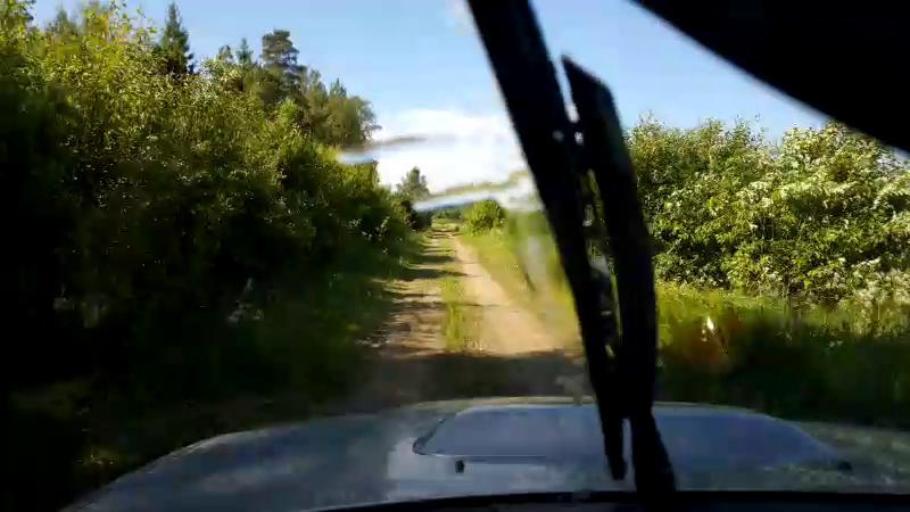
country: EE
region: Paernumaa
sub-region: Sindi linn
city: Sindi
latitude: 58.5073
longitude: 24.6456
